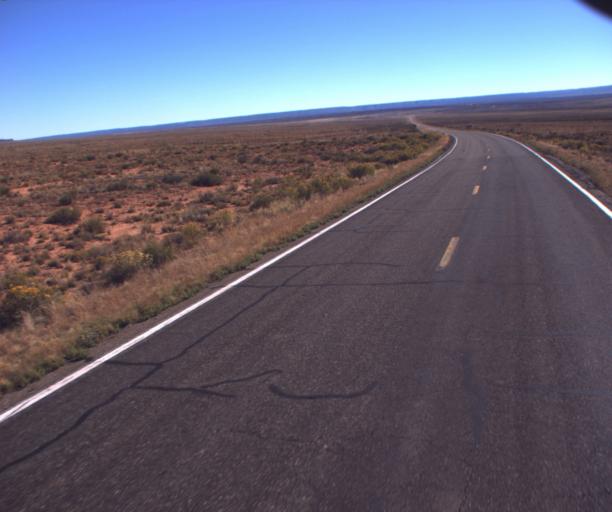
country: US
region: Arizona
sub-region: Coconino County
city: Fredonia
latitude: 36.9290
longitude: -112.4880
